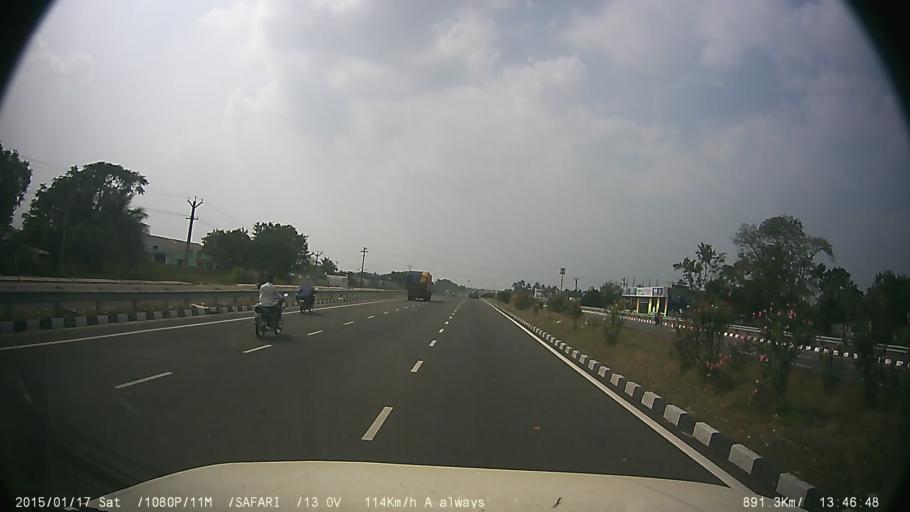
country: IN
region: Tamil Nadu
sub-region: Vellore
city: Vellore
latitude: 12.9146
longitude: 79.0745
